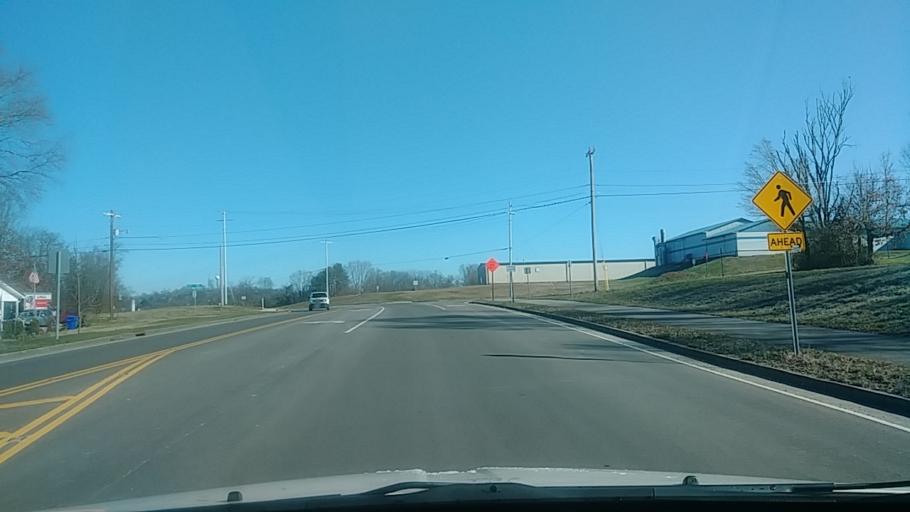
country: US
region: Tennessee
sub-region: Hamblen County
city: Morristown
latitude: 36.1982
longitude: -83.3094
